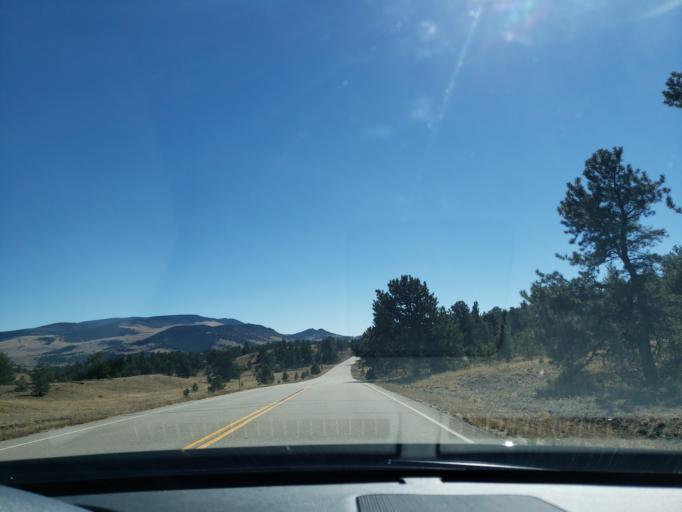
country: US
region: Colorado
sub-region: Chaffee County
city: Buena Vista
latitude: 38.8904
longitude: -105.6860
